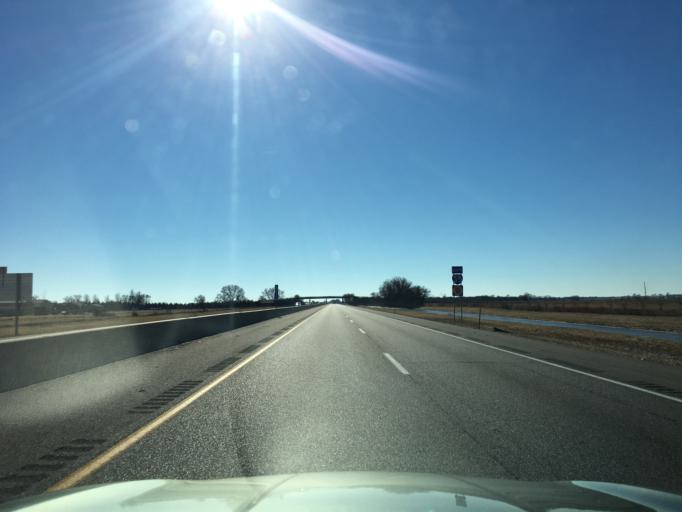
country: US
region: Kansas
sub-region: Sumner County
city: Mulvane
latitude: 37.4694
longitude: -97.3228
